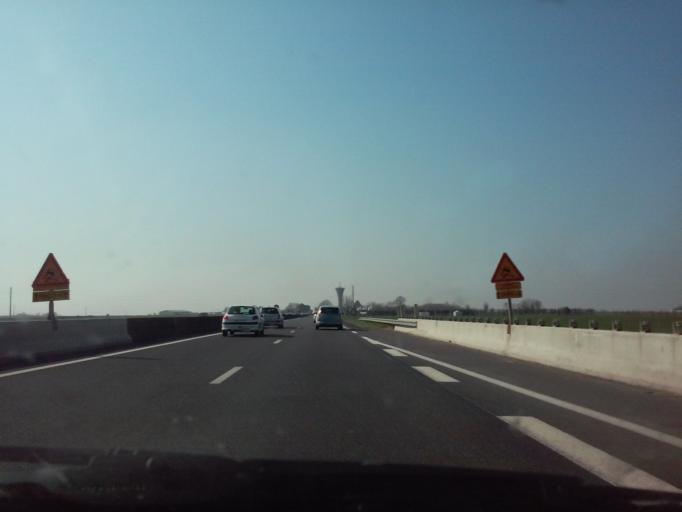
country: FR
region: Lower Normandy
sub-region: Departement du Calvados
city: Creully
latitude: 49.2359
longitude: -0.5860
